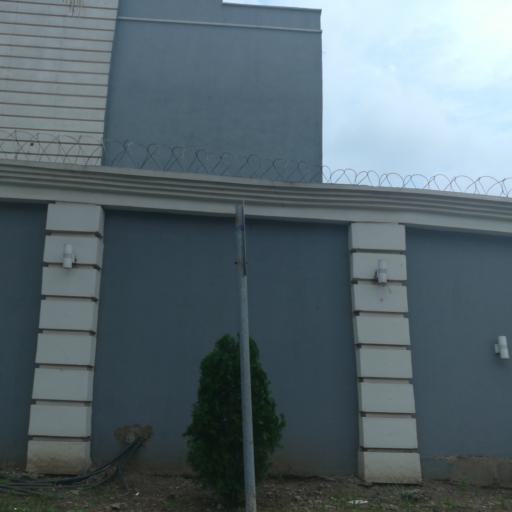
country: NG
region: Lagos
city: Ojota
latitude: 6.5766
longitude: 3.3936
